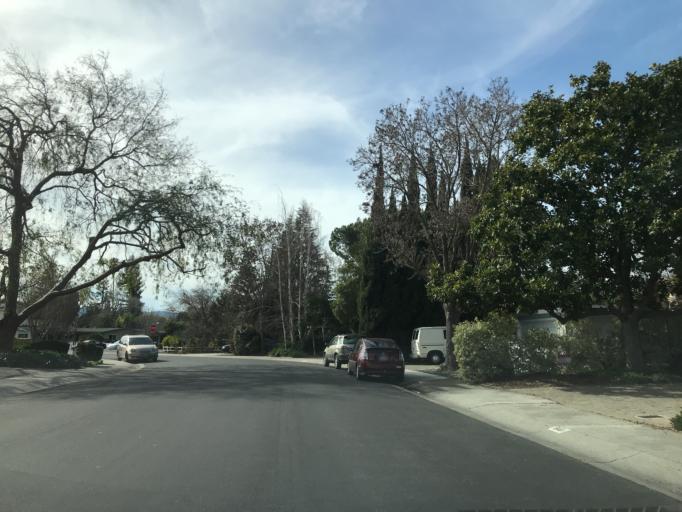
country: US
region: California
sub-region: Santa Clara County
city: Palo Alto
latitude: 37.4250
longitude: -122.1197
